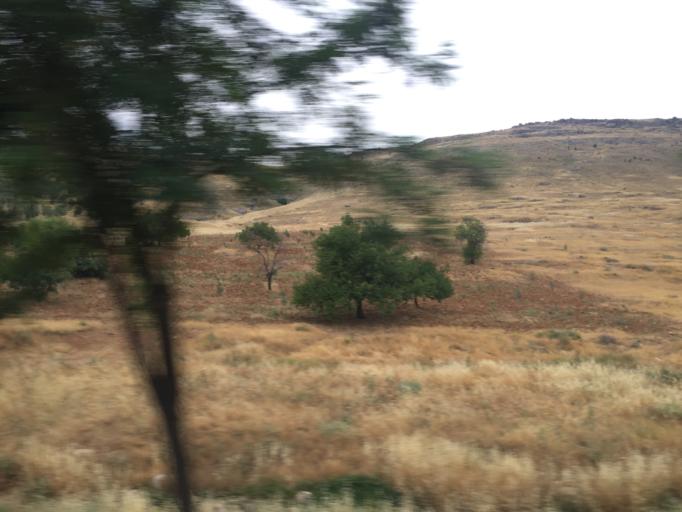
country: TR
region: Gaziantep
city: Yesildere
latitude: 36.9934
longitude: 37.4470
